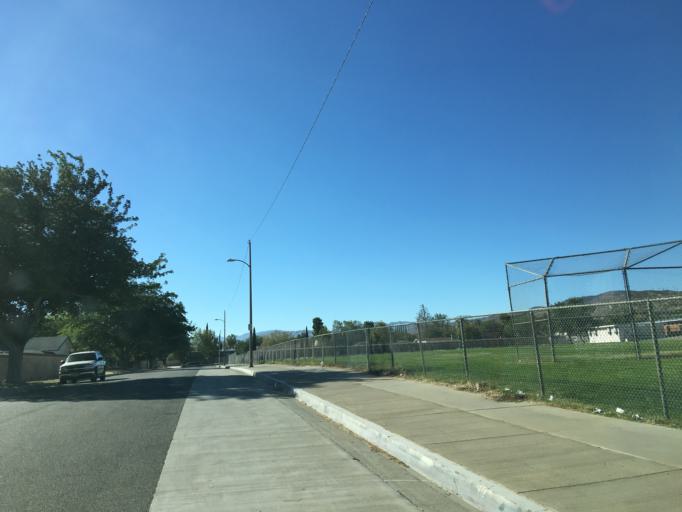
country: US
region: California
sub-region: Los Angeles County
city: Desert View Highlands
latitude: 34.5951
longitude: -118.1532
